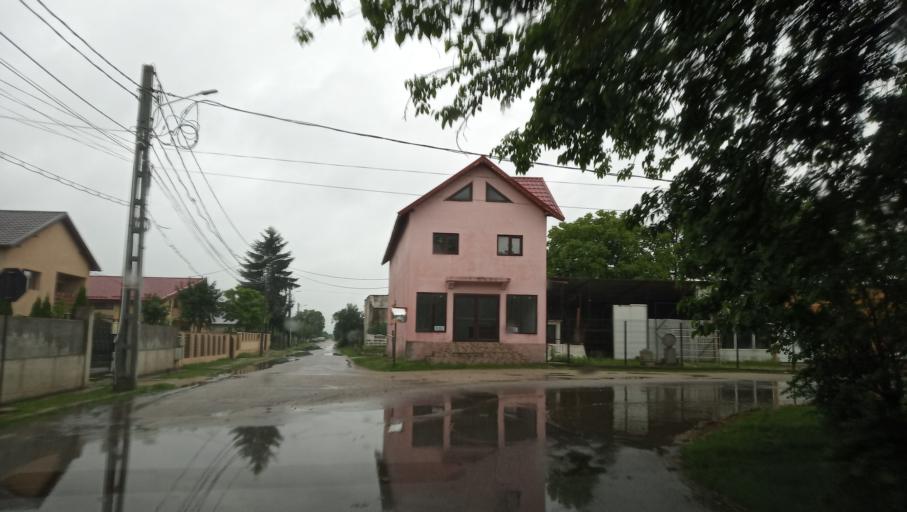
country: RO
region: Dambovita
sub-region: Oras Gaesti
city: Gaesti
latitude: 44.7156
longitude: 25.3319
